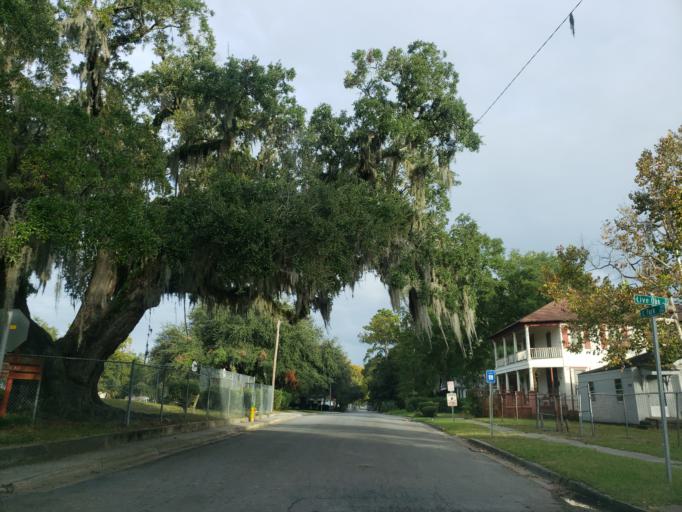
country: US
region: Georgia
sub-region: Chatham County
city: Savannah
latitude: 32.0601
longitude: -81.0792
